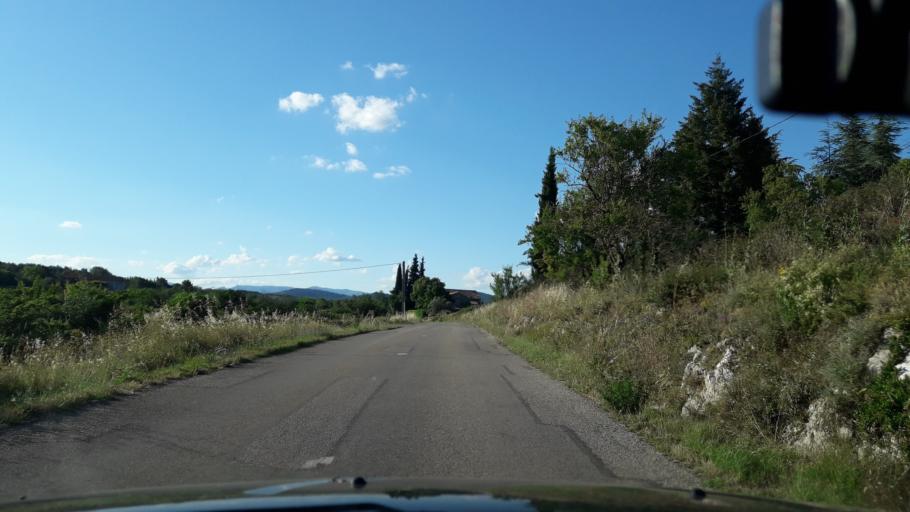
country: FR
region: Rhone-Alpes
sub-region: Departement de l'Ardeche
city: Lavilledieu
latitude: 44.5882
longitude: 4.4607
